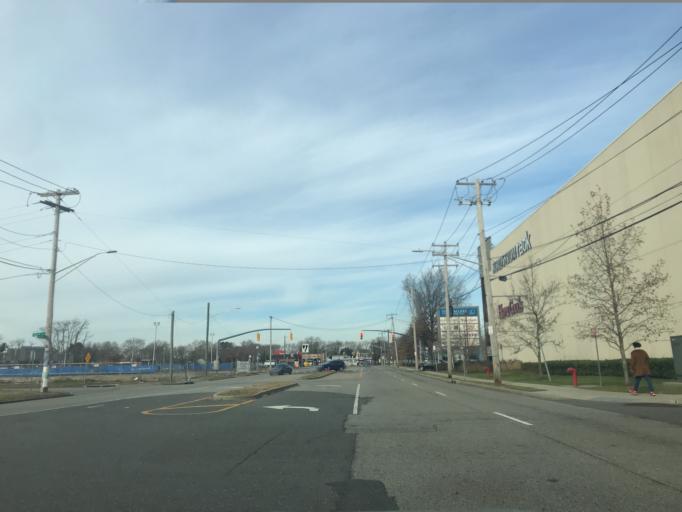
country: US
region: New York
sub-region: Nassau County
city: Carle Place
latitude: 40.7419
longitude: -73.6064
